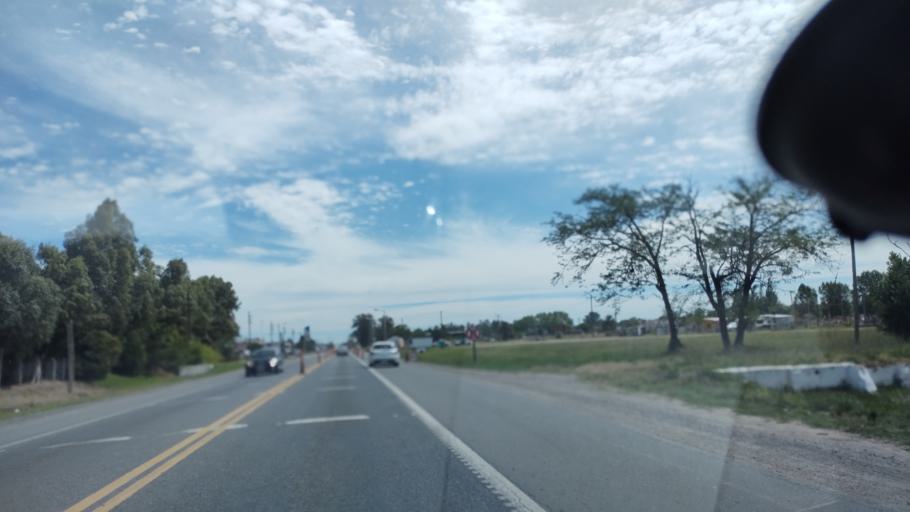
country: AR
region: Buenos Aires
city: Canuelas
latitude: -35.0387
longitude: -58.7595
